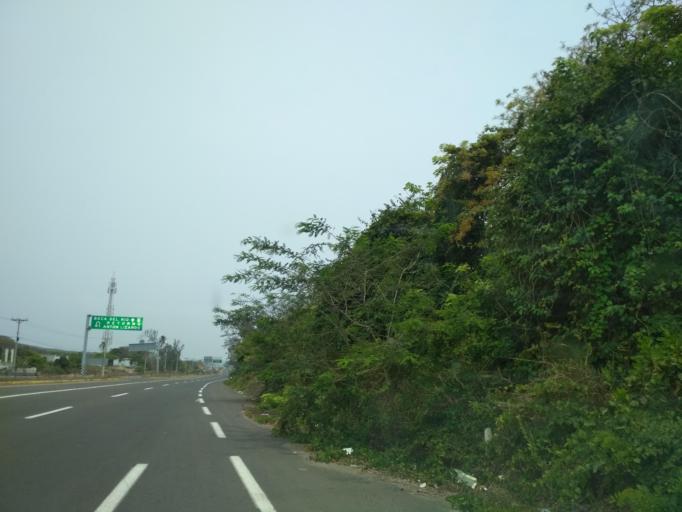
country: MX
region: Veracruz
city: Anton Lizardo
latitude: 19.0518
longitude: -96.0150
